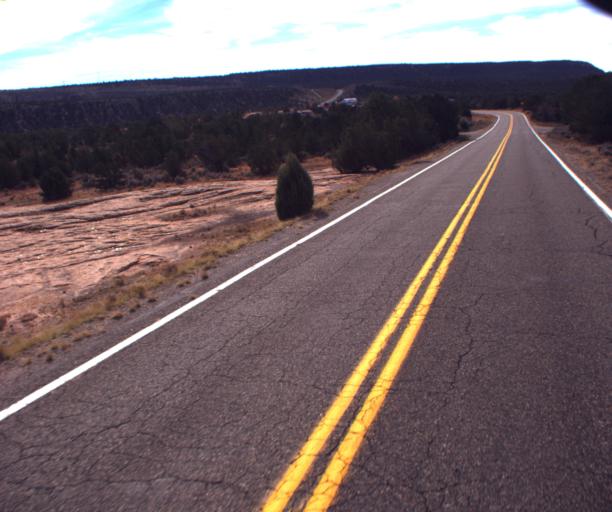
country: US
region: Arizona
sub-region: Navajo County
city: Kayenta
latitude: 36.5661
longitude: -110.5020
